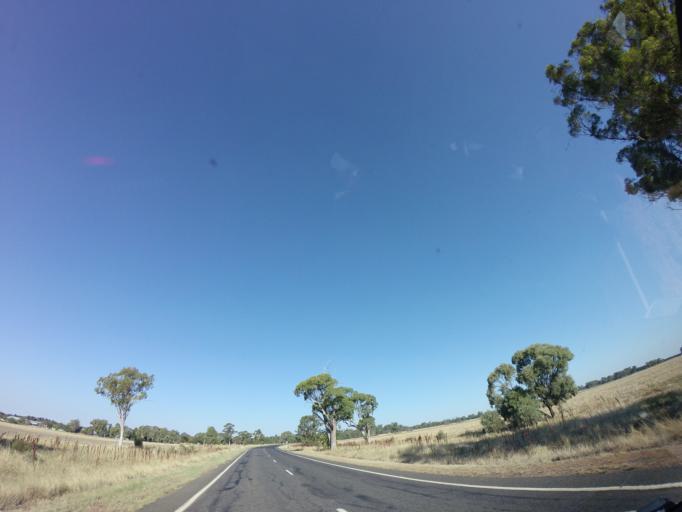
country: AU
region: New South Wales
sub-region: Gilgandra
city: Gilgandra
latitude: -31.7046
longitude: 148.6258
